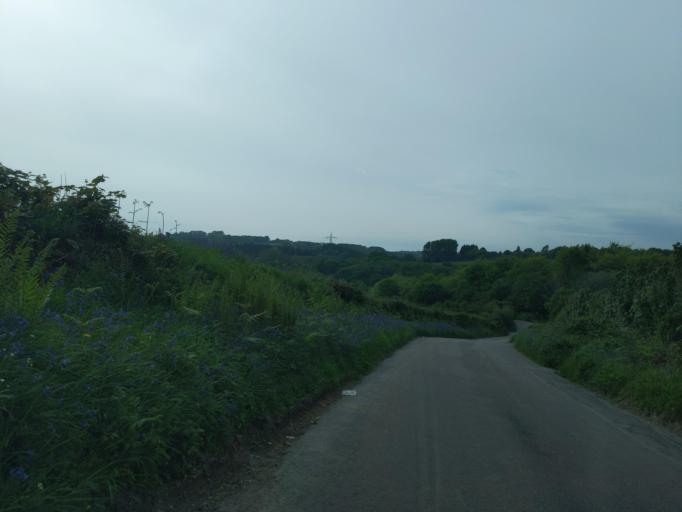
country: GB
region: England
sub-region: Devon
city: Plympton
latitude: 50.4352
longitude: -4.0729
